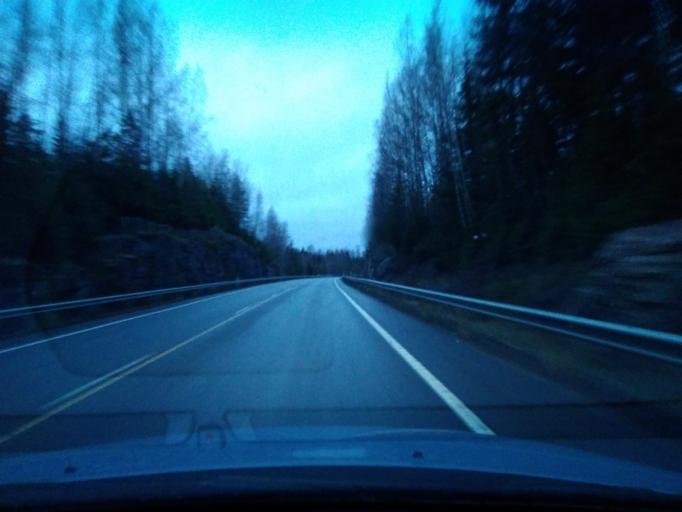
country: FI
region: Uusimaa
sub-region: Porvoo
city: Porvoo
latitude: 60.4064
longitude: 25.5874
